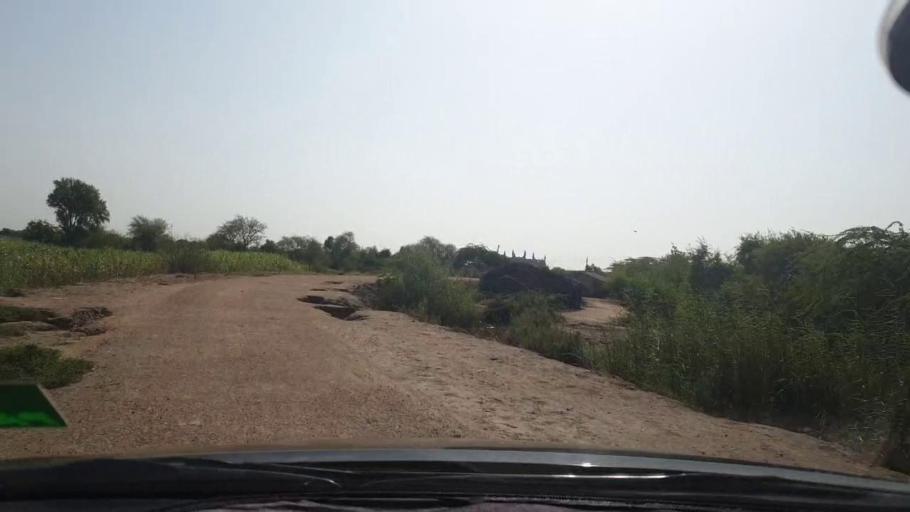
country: PK
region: Sindh
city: Tando Bago
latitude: 24.6959
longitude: 69.0208
